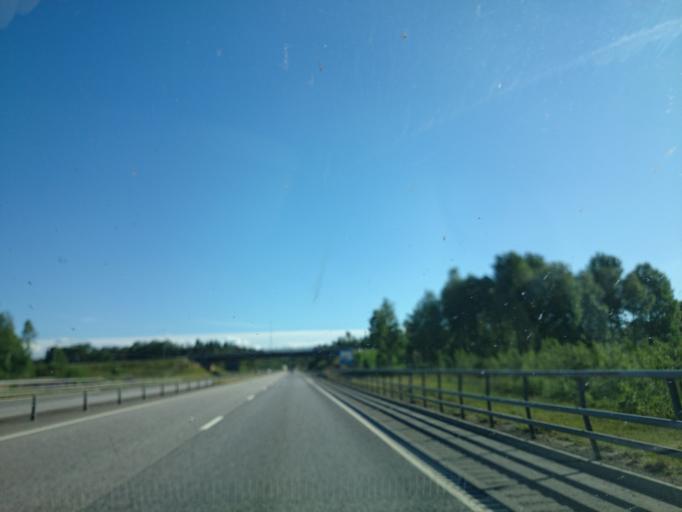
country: SE
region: Kronoberg
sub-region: Markaryds Kommun
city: Markaryd
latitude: 56.4622
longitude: 13.6276
